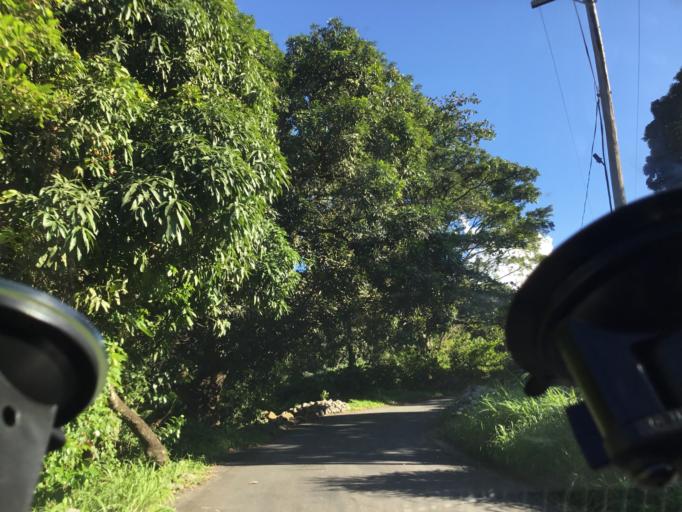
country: VC
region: Saint David
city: Chateaubelair
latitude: 13.3005
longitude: -61.2279
